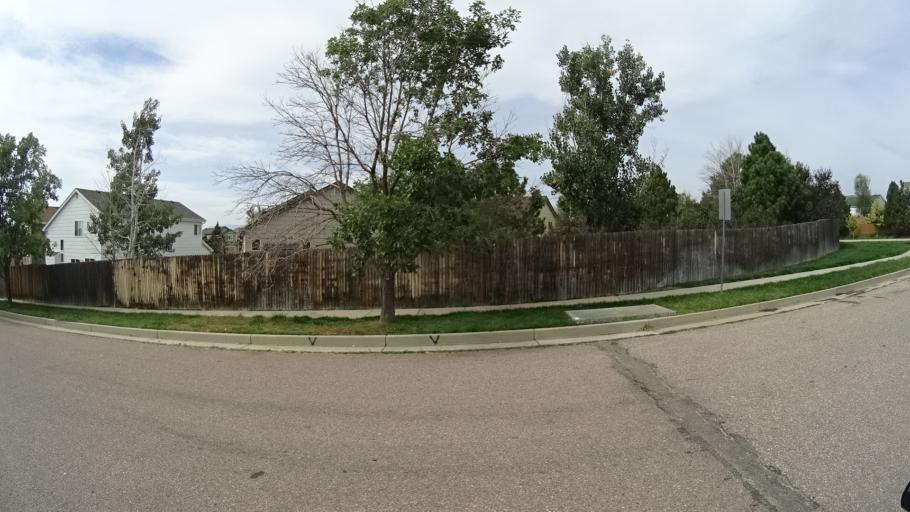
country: US
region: Colorado
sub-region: El Paso County
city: Cimarron Hills
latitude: 38.9113
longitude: -104.7050
